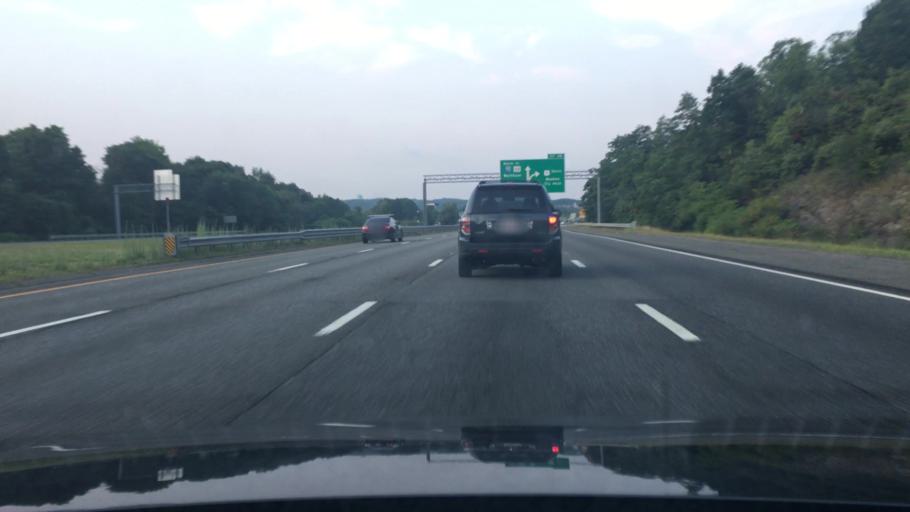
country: US
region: Massachusetts
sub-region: Essex County
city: Danvers
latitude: 42.5681
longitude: -70.9711
